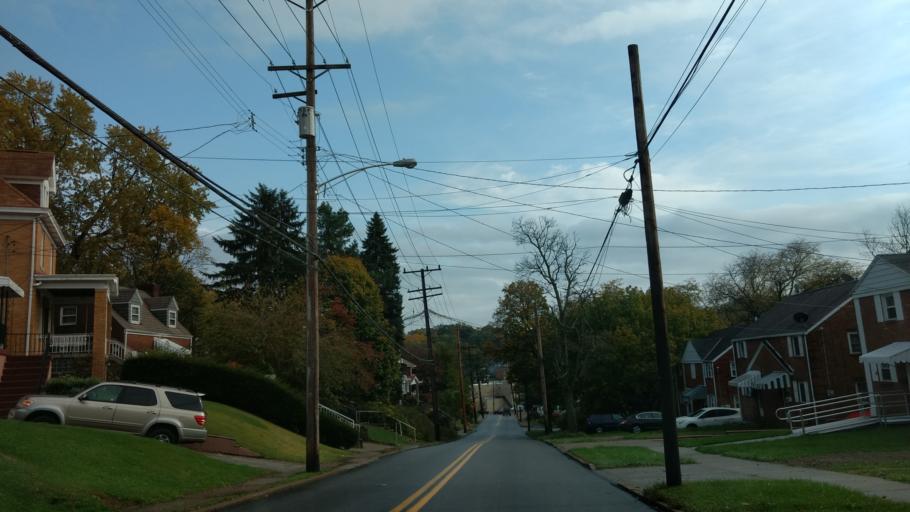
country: US
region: Pennsylvania
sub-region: Allegheny County
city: Dormont
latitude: 40.3995
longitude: -80.0298
